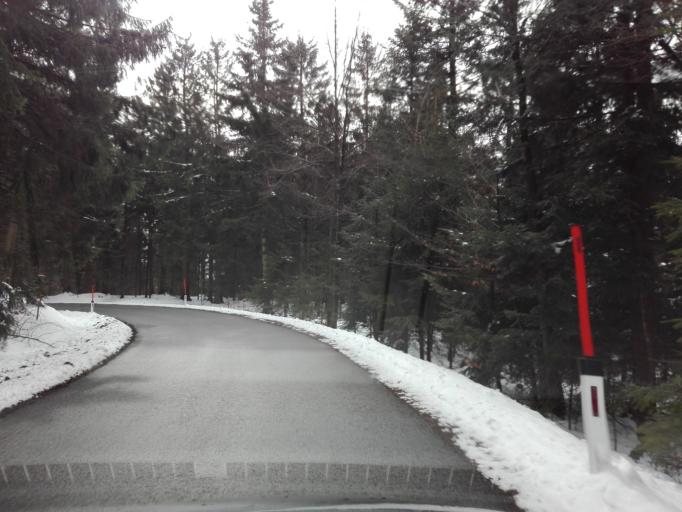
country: AT
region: Upper Austria
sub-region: Politischer Bezirk Rohrbach
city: Pfarrkirchen im Muehlkreis
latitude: 48.5537
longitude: 13.8308
